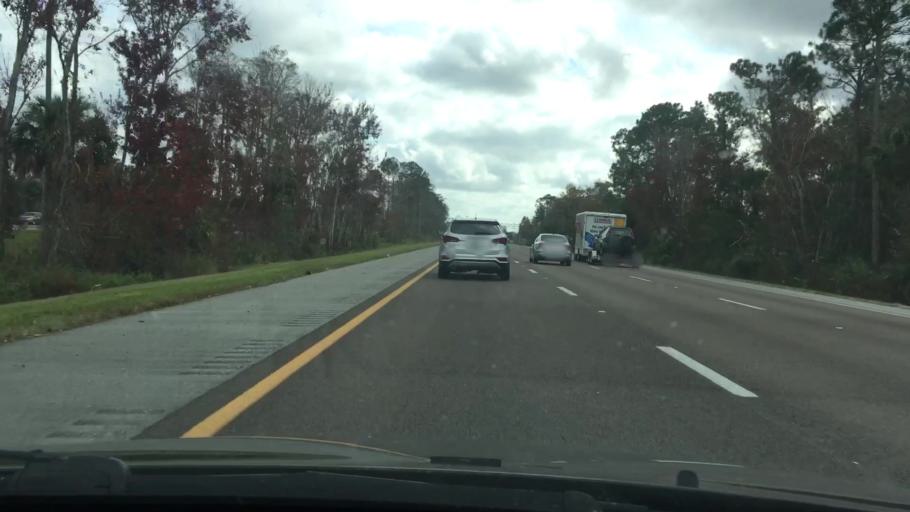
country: US
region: Florida
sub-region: Volusia County
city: Glencoe
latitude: 28.9727
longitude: -80.9620
